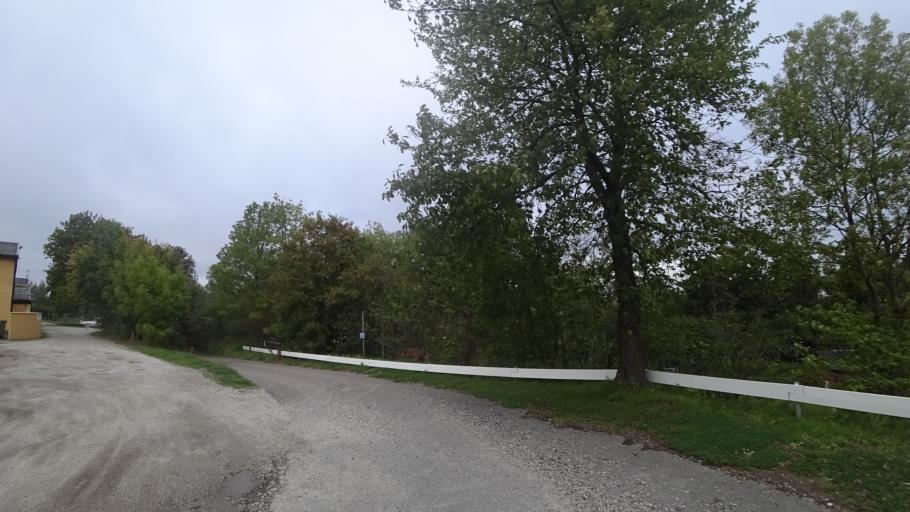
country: SE
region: Skane
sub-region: Kavlinge Kommun
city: Kaevlinge
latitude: 55.7847
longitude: 13.1137
